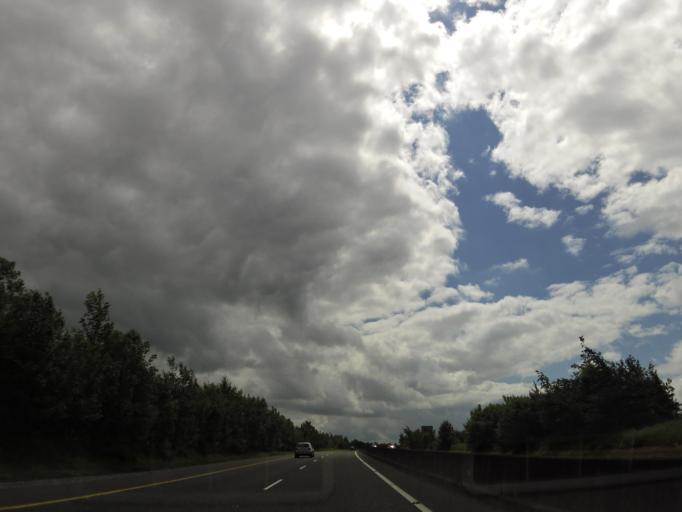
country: IE
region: Munster
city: Cashel
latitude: 52.5325
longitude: -7.8598
